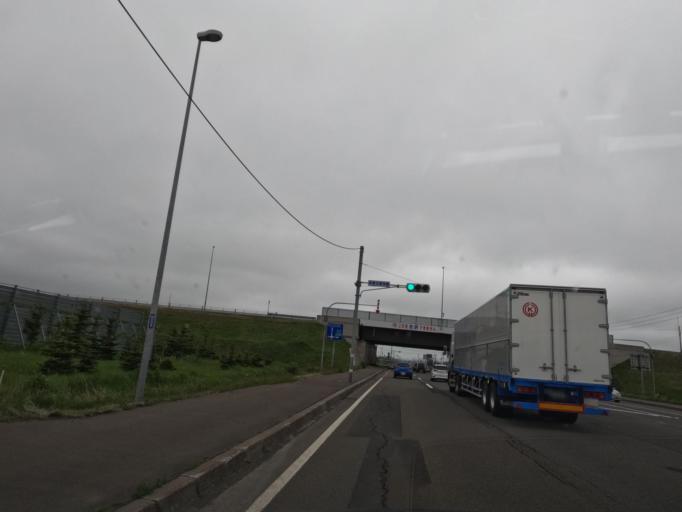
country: JP
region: Hokkaido
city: Tobetsu
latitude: 43.1831
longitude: 141.5232
